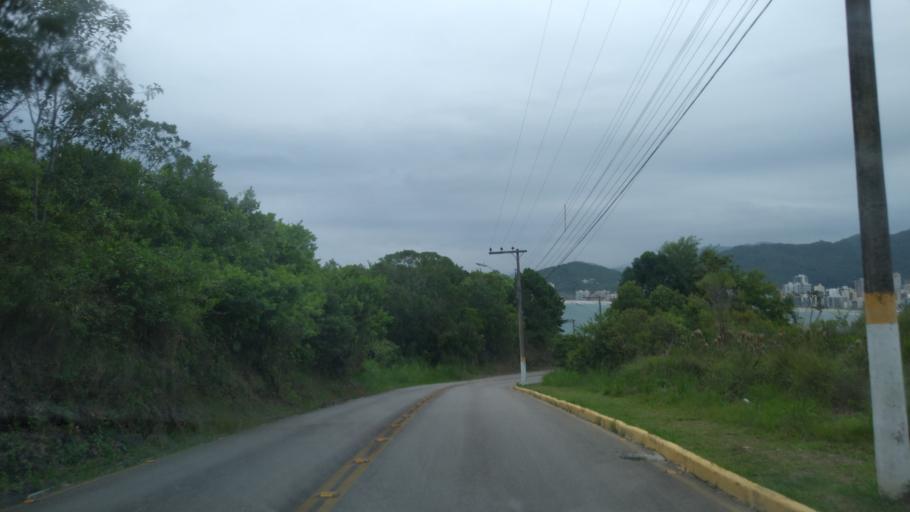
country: BR
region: Santa Catarina
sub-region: Itapema
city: Itapema
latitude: -27.0890
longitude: -48.6022
